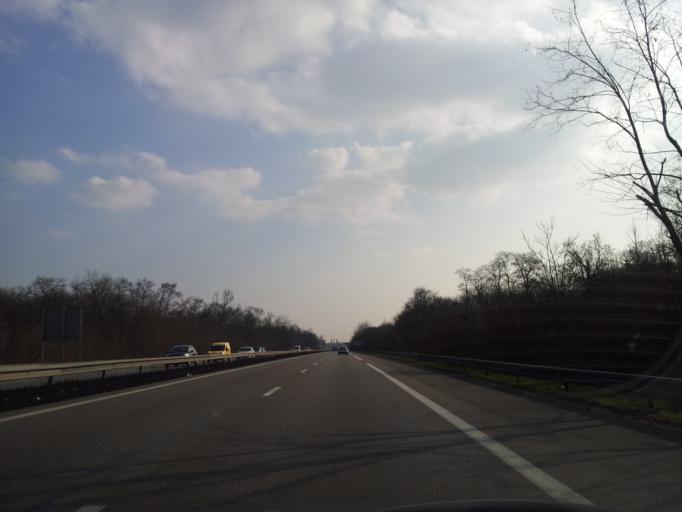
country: FR
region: Alsace
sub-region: Departement du Haut-Rhin
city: Sainte-Croix-en-Plaine
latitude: 48.0368
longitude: 7.3711
